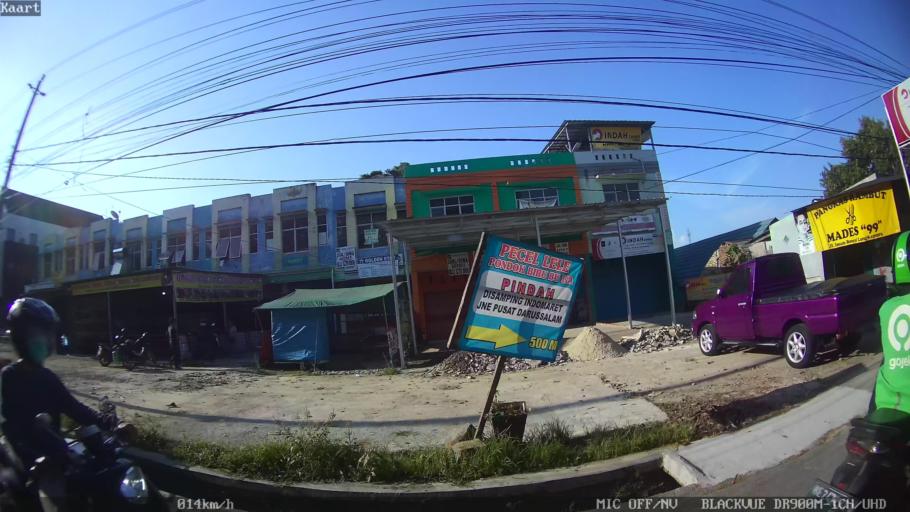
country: ID
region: Lampung
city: Kedaton
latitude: -5.3927
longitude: 105.2268
